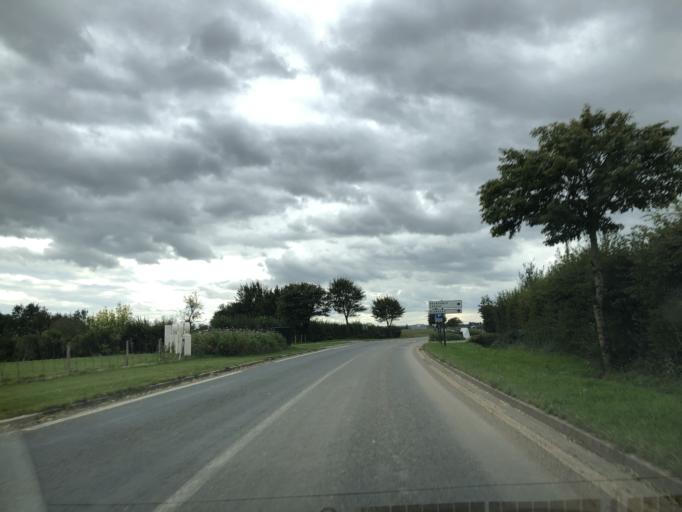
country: FR
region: Nord-Pas-de-Calais
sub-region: Departement du Pas-de-Calais
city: Fruges
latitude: 50.4806
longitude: 2.1191
